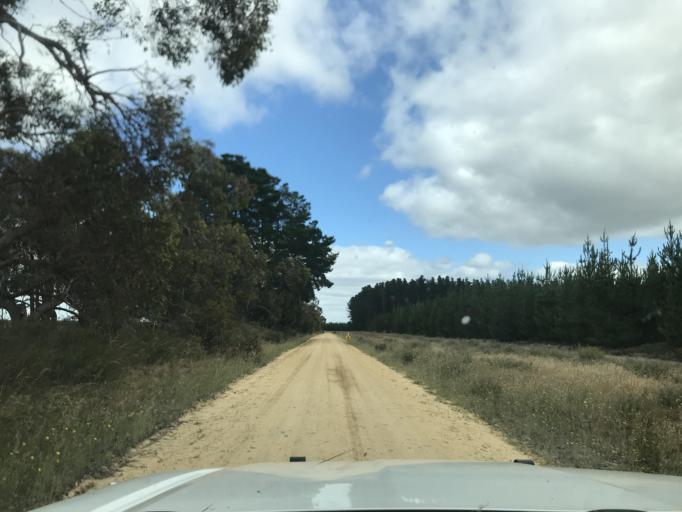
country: AU
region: South Australia
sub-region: Wattle Range
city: Penola
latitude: -37.3167
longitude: 141.1329
